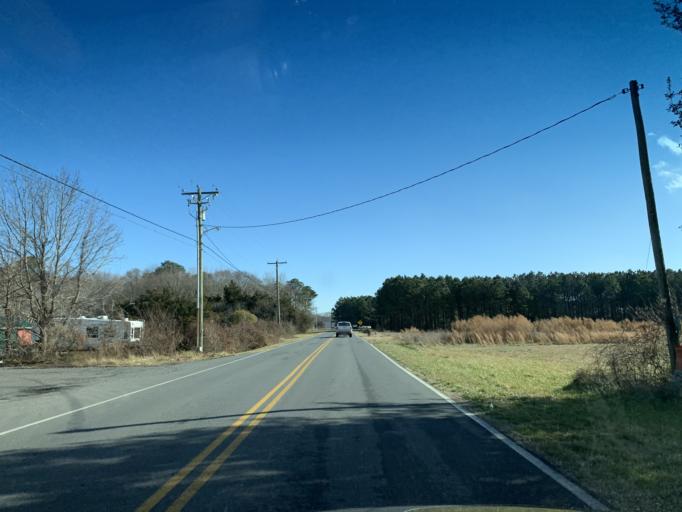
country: US
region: Maryland
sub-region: Worcester County
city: Ocean Pines
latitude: 38.4185
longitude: -75.1404
